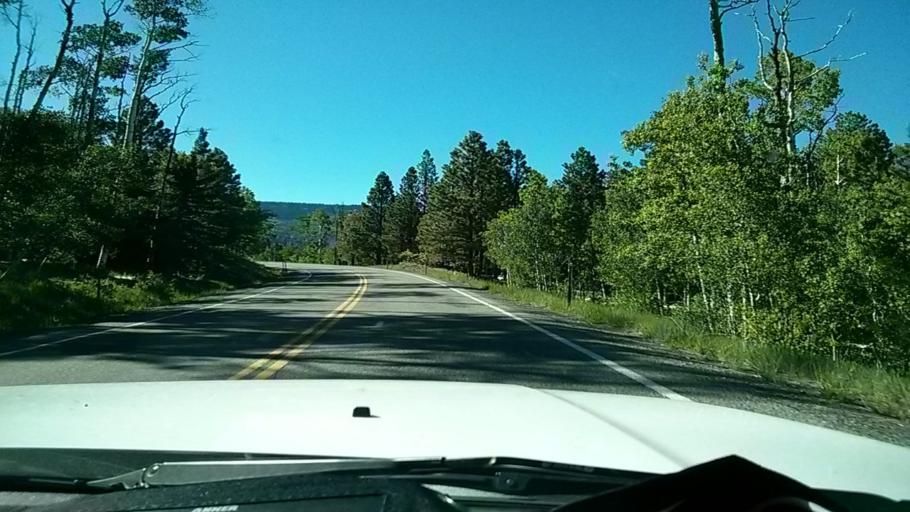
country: US
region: Utah
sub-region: Wayne County
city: Loa
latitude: 38.0847
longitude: -111.3368
